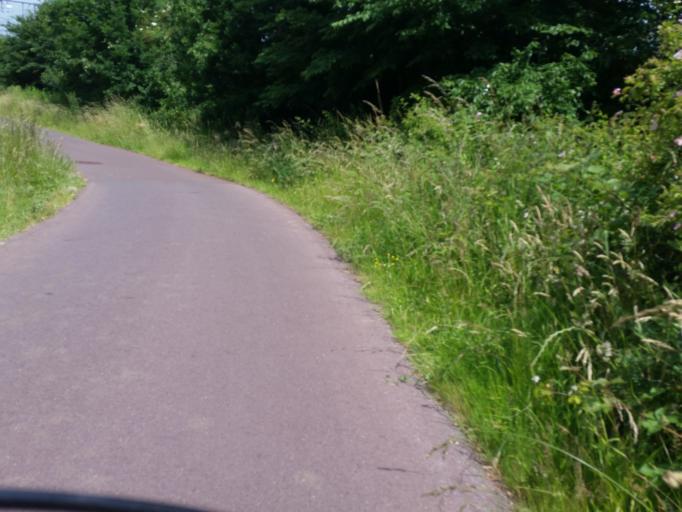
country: BE
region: Flanders
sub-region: Provincie Antwerpen
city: Hove
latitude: 51.1389
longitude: 4.4735
